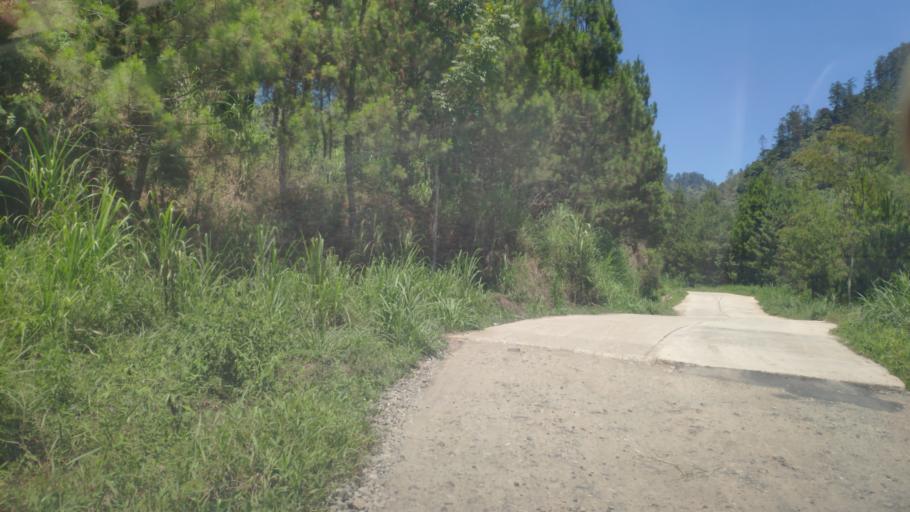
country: ID
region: Central Java
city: Buaran
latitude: -7.2354
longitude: 109.6428
